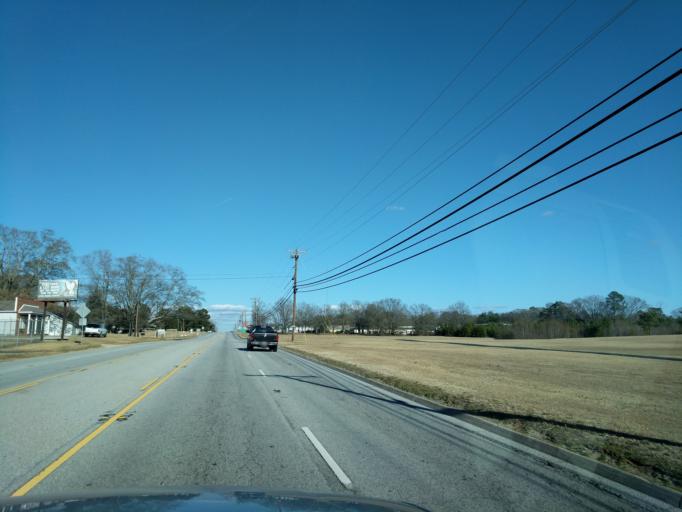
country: US
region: South Carolina
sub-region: Greenwood County
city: Greenwood
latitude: 34.2193
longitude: -82.1246
